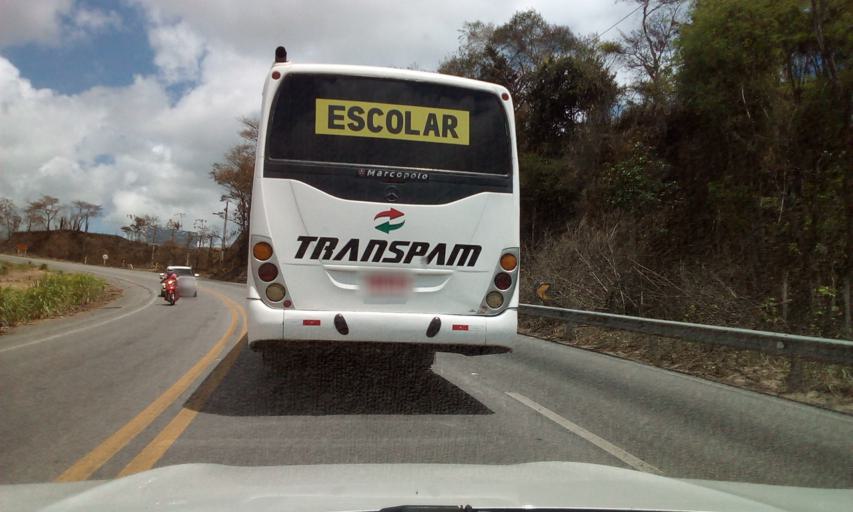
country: BR
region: Alagoas
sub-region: Sao Miguel Dos Campos
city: Sao Miguel dos Campos
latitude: -9.7705
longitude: -36.0768
